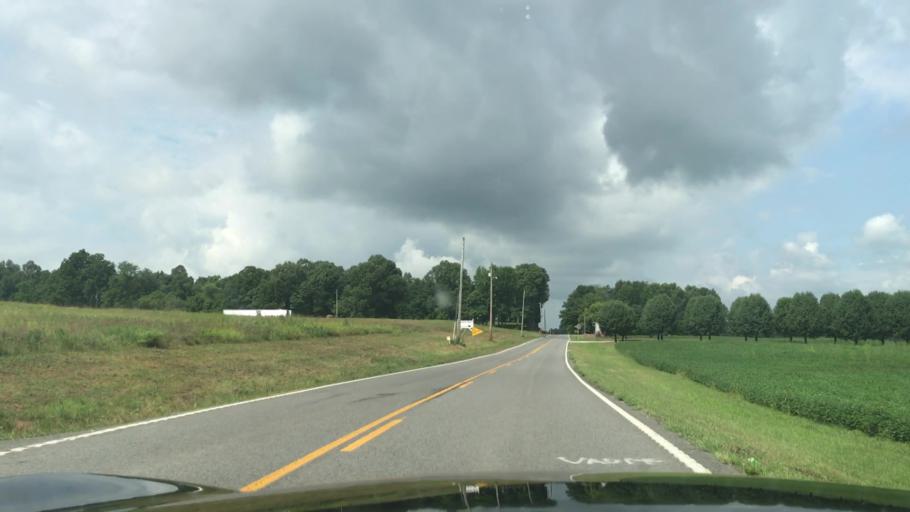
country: US
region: Kentucky
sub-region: Muhlenberg County
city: Greenville
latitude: 37.1977
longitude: -87.1139
